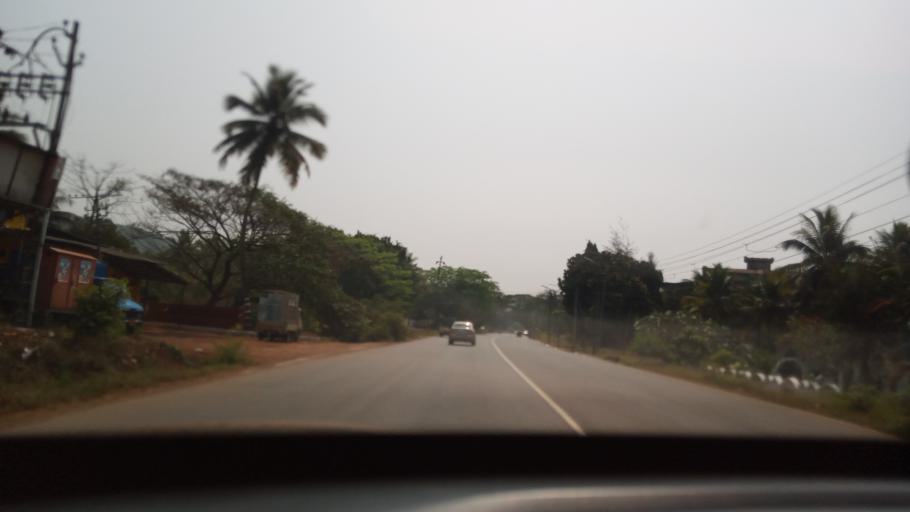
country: IN
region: Goa
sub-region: South Goa
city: Raia
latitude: 15.3241
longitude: 73.9382
